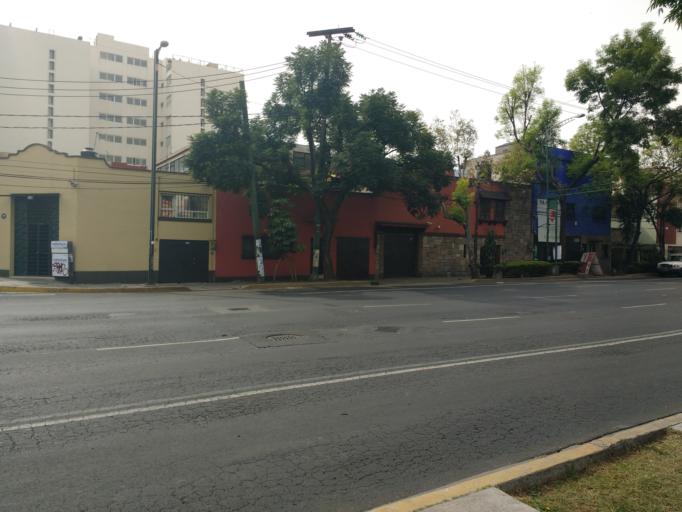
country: MX
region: Mexico City
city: Coyoacan
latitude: 19.3616
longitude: -99.1522
